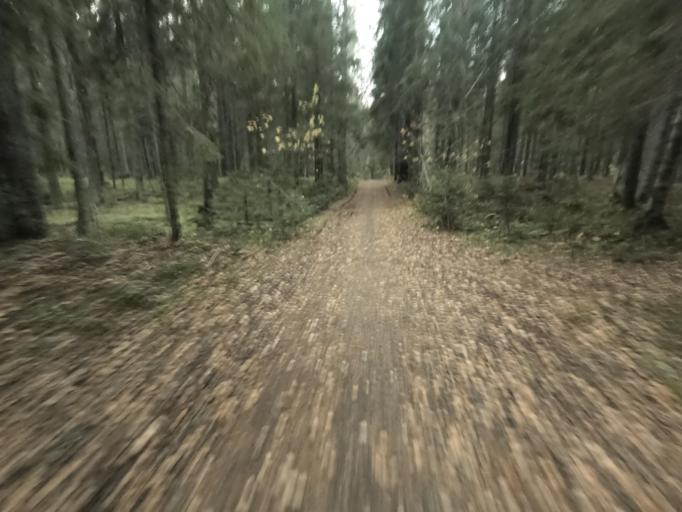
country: RU
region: Leningrad
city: Leninskoye
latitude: 60.1973
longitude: 29.8465
